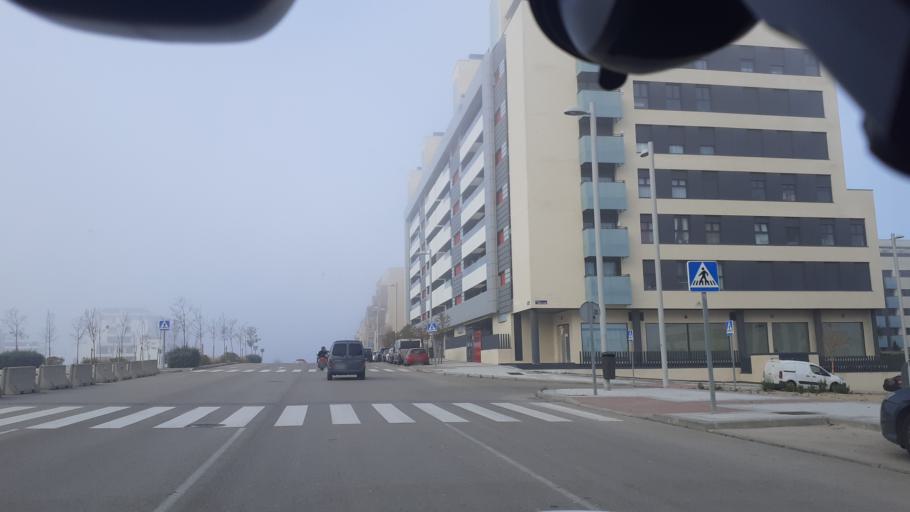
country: ES
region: Madrid
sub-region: Provincia de Madrid
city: Coslada
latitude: 40.4061
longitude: -3.5525
